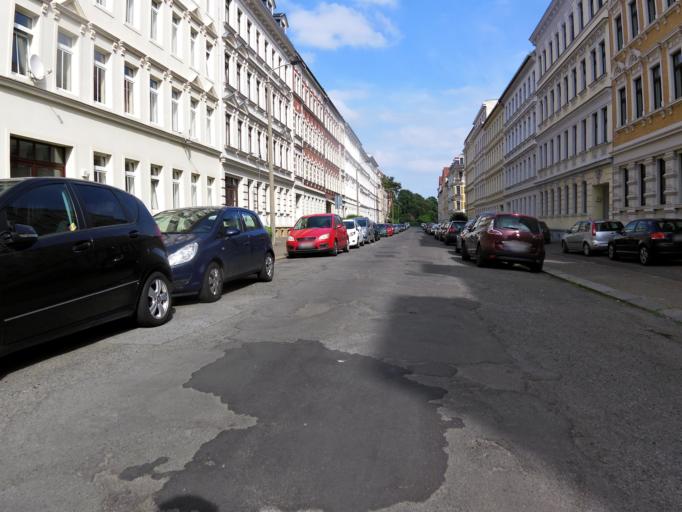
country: DE
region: Saxony
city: Leipzig
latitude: 51.3644
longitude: 12.3663
